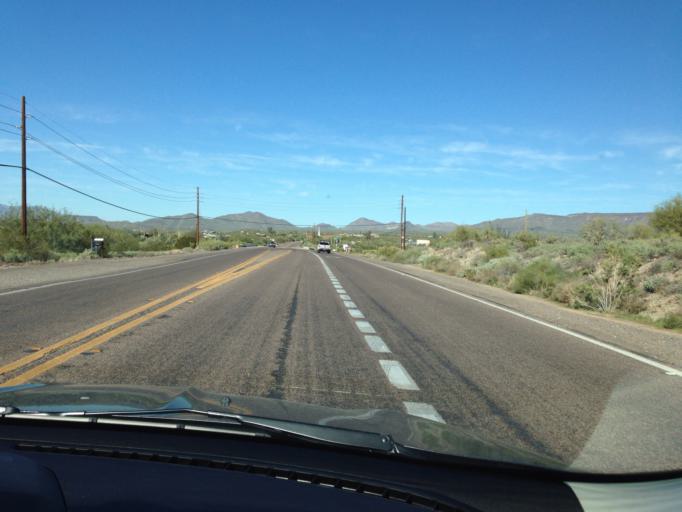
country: US
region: Arizona
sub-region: Maricopa County
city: New River
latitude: 33.8835
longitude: -112.0723
